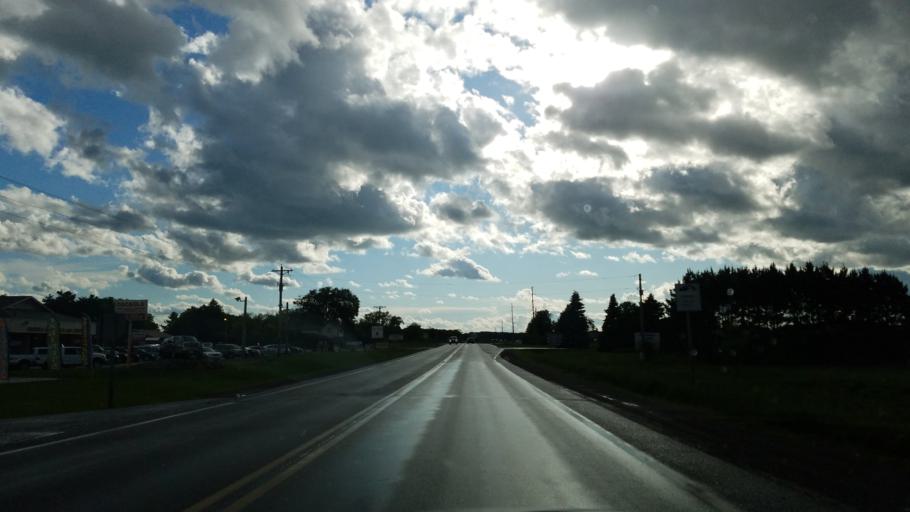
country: US
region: Wisconsin
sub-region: Polk County
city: Osceola
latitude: 45.3432
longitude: -92.6487
